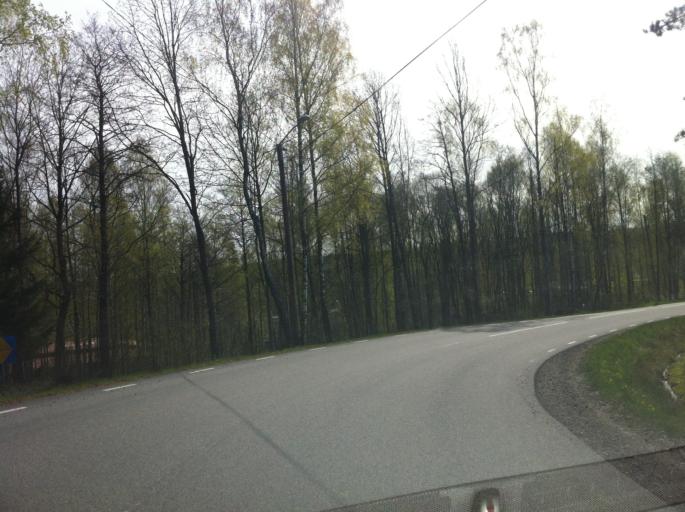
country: SE
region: Vaestra Goetaland
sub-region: Marks Kommun
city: Fritsla
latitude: 57.3503
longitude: 12.8881
